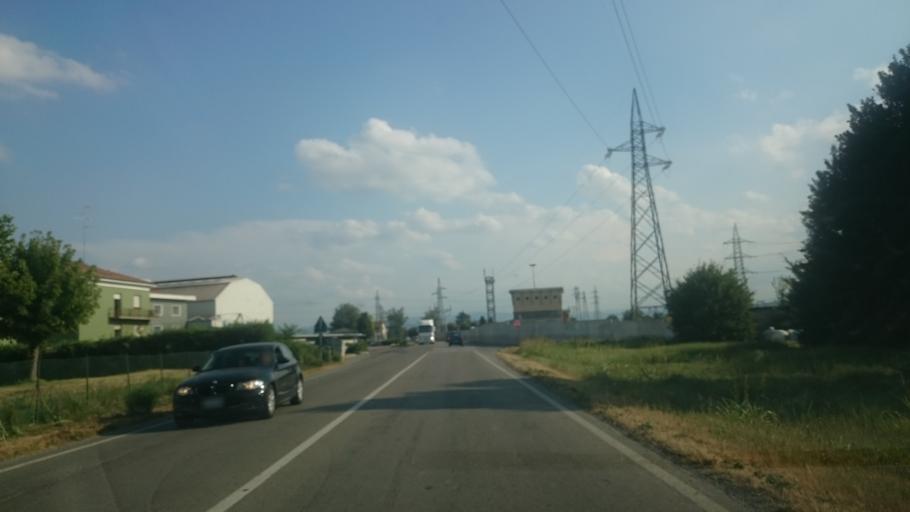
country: IT
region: Emilia-Romagna
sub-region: Provincia di Reggio Emilia
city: Rubiera
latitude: 44.6288
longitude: 10.7774
